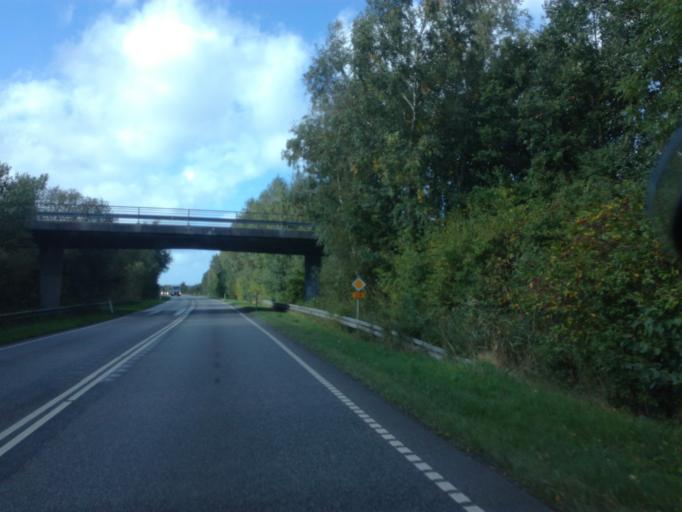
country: DK
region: South Denmark
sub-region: Fredericia Kommune
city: Fredericia
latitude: 55.6250
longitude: 9.7316
